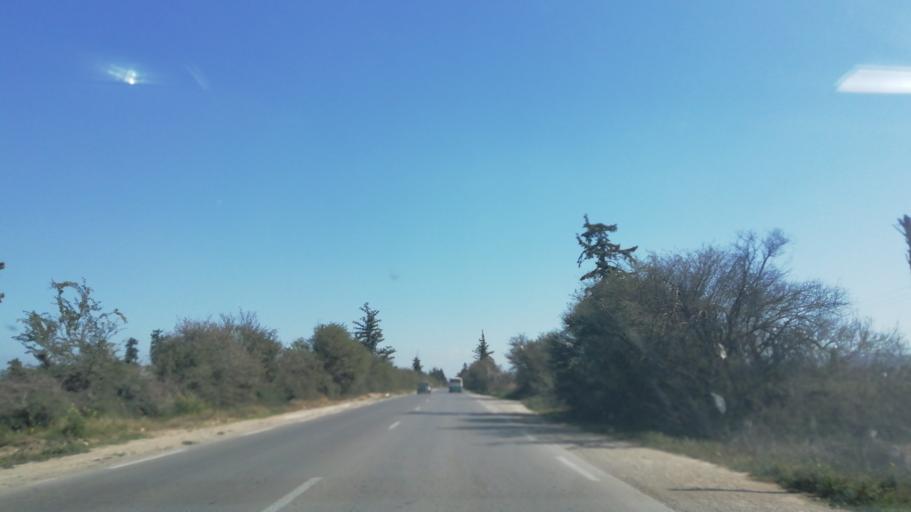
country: DZ
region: Mascara
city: Sig
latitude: 35.5708
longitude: -0.0373
